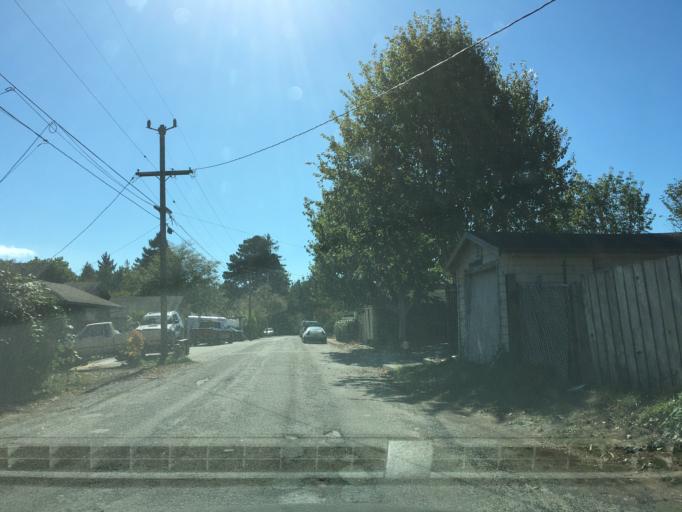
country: US
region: California
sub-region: Humboldt County
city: Myrtletown
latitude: 40.7869
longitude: -124.1387
